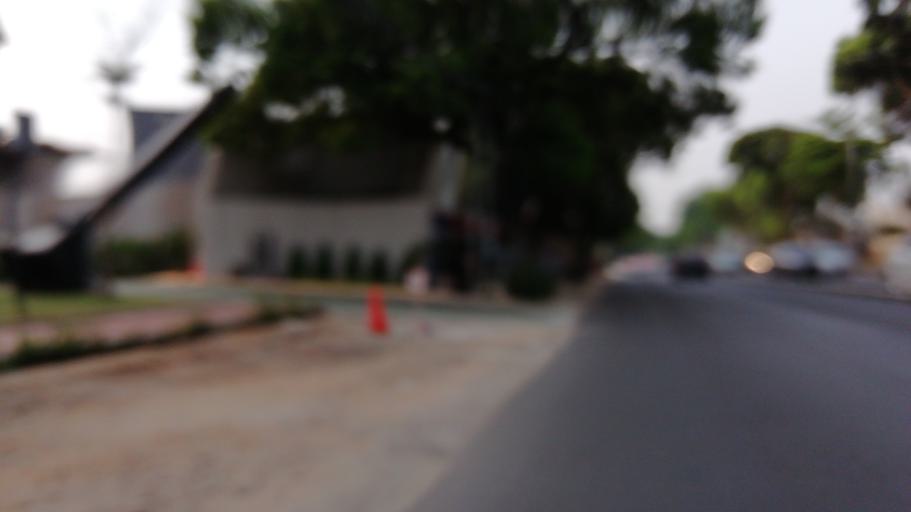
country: ID
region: Jakarta Raya
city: Jakarta
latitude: -6.2849
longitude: 106.8071
